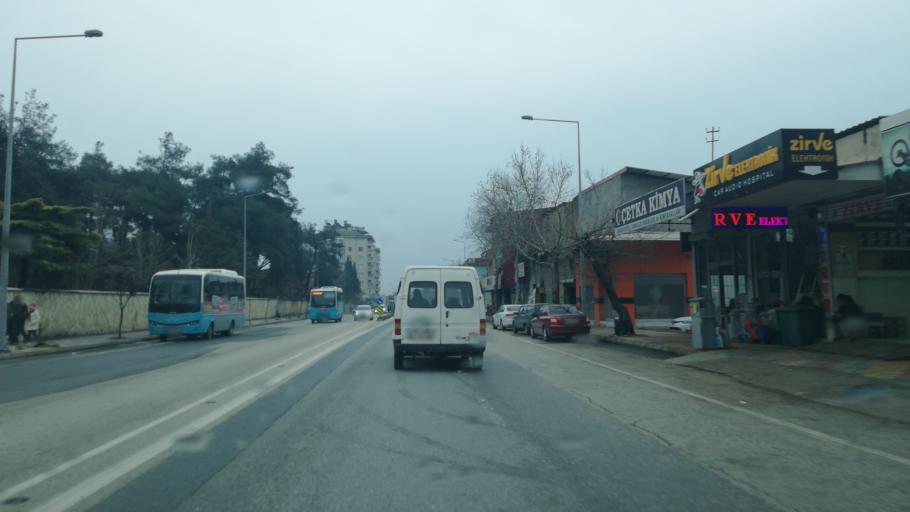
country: TR
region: Kahramanmaras
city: Kahramanmaras
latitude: 37.5737
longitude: 36.9386
